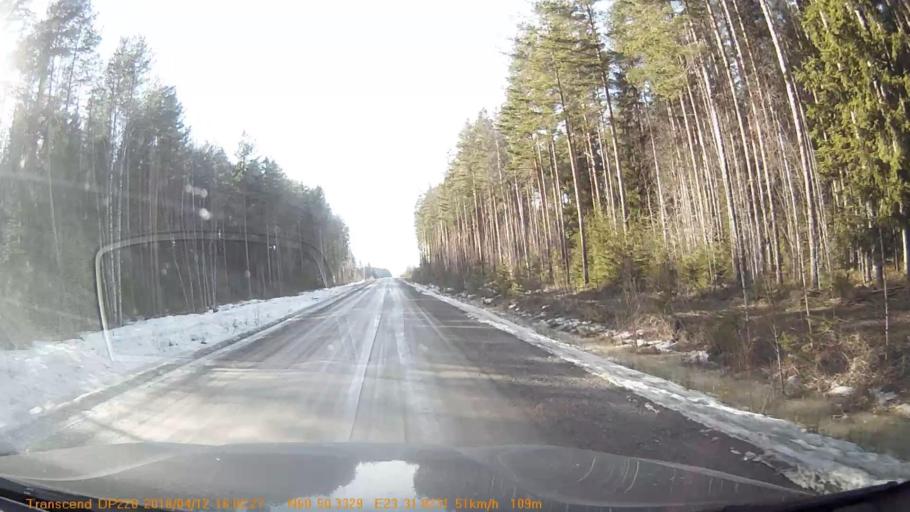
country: FI
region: Haeme
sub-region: Forssa
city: Jokioinen
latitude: 60.8391
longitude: 23.5293
